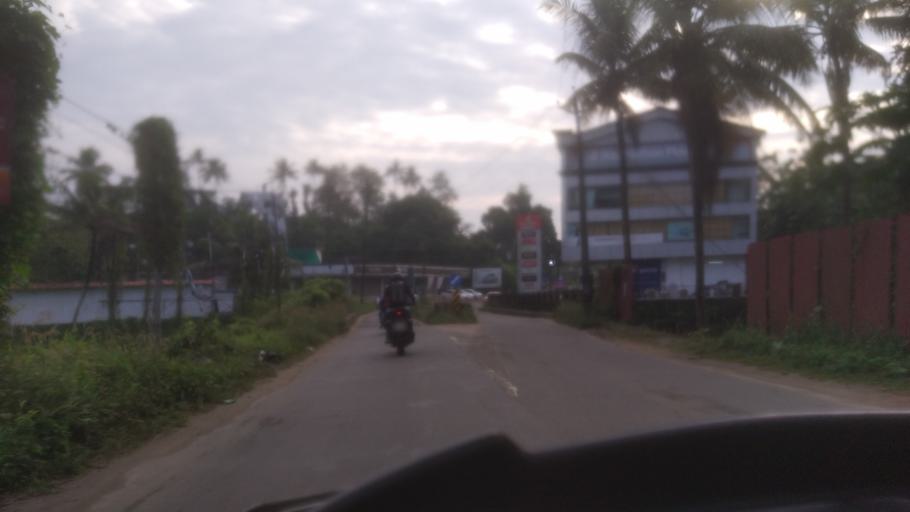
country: IN
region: Kerala
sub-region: Ernakulam
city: Kotamangalam
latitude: 10.0679
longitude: 76.6232
